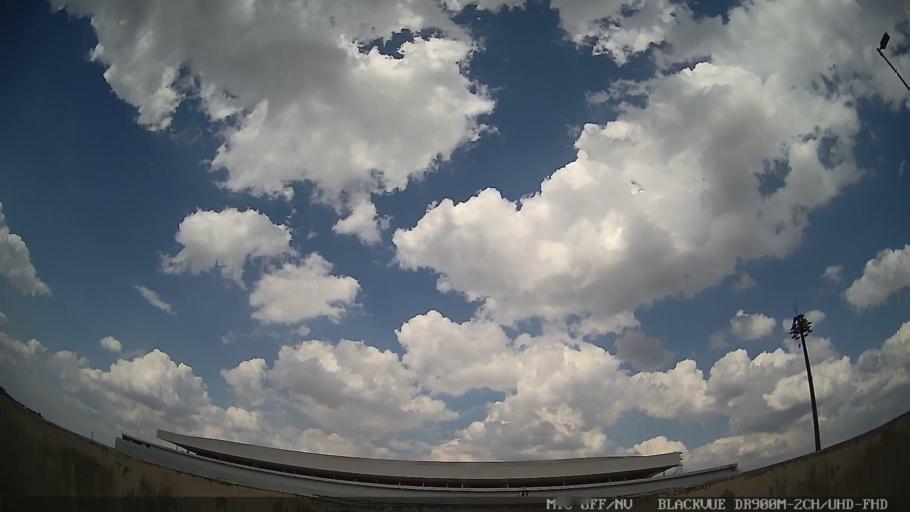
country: BR
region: Sao Paulo
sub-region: Guarulhos
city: Guarulhos
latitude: -23.5470
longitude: -46.4765
